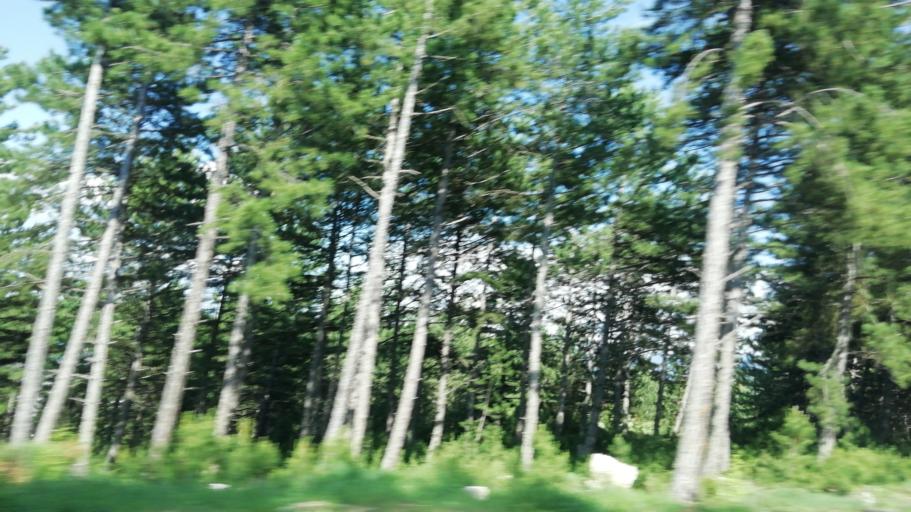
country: TR
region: Karabuk
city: Karabuk
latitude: 41.1215
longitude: 32.6053
